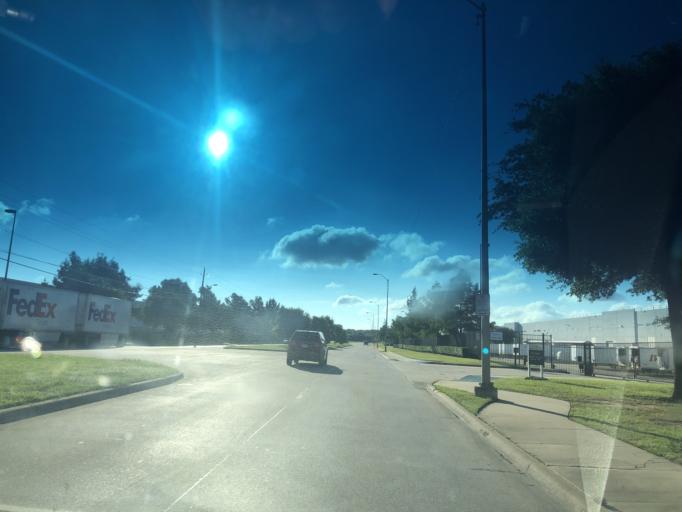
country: US
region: Texas
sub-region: Dallas County
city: Grand Prairie
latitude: 32.7984
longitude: -97.0000
